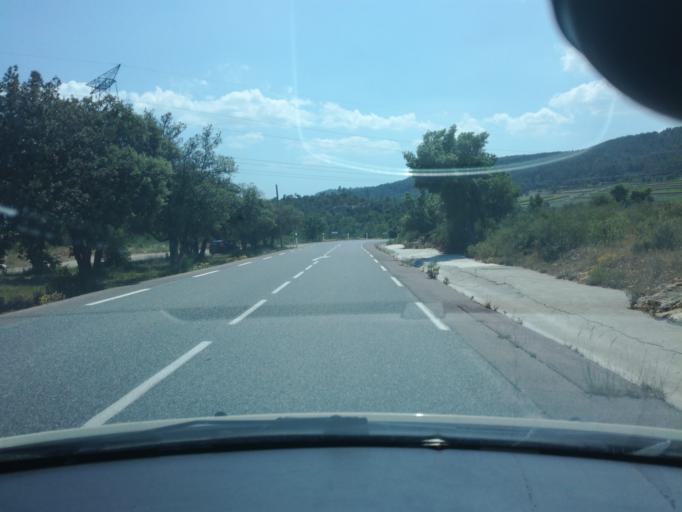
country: FR
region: Provence-Alpes-Cote d'Azur
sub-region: Departement du Var
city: La Motte
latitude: 43.5346
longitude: 6.5720
